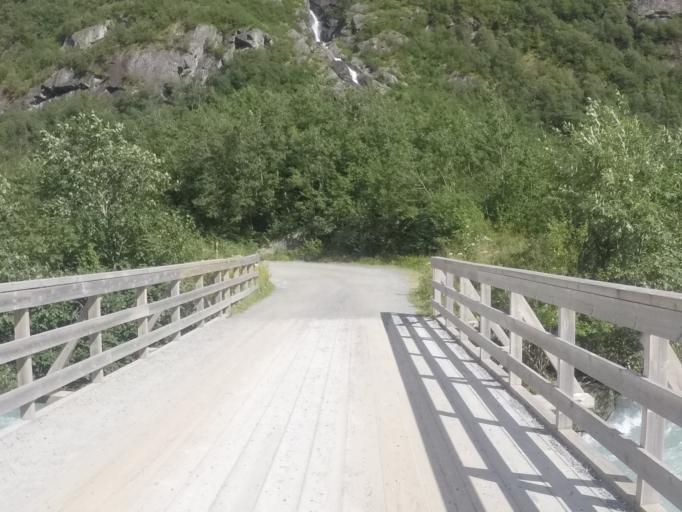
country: NO
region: Sogn og Fjordane
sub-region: Stryn
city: Stryn
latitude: 61.7587
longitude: 7.0393
